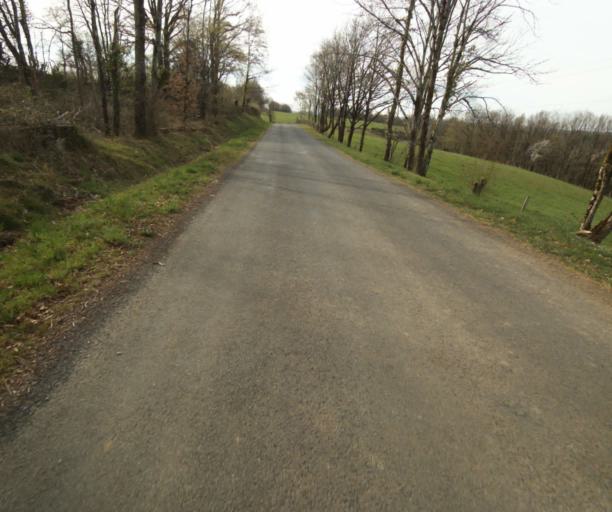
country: FR
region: Limousin
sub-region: Departement de la Correze
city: Seilhac
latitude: 45.4119
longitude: 1.7835
